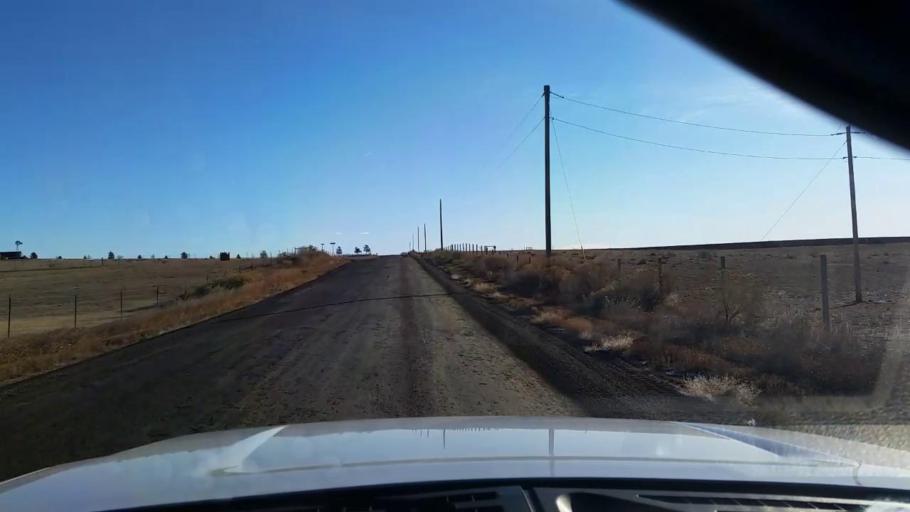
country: US
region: Colorado
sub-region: Larimer County
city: Wellington
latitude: 40.7696
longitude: -105.1112
